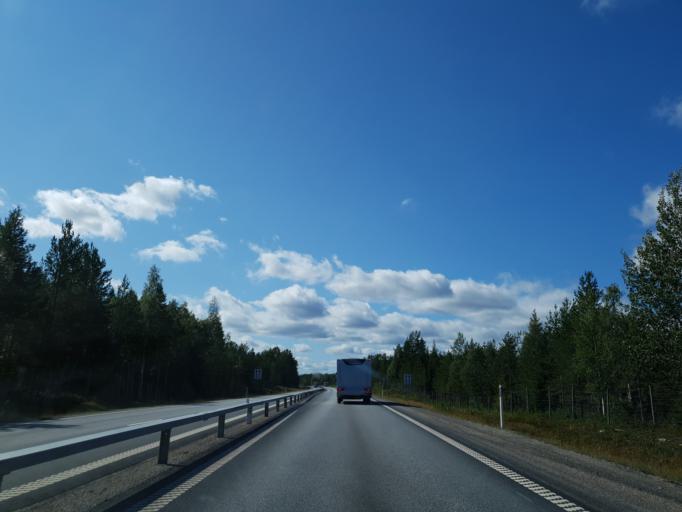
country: SE
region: Vaesterbotten
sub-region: Umea Kommun
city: Hoernefors
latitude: 63.6254
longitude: 19.8530
